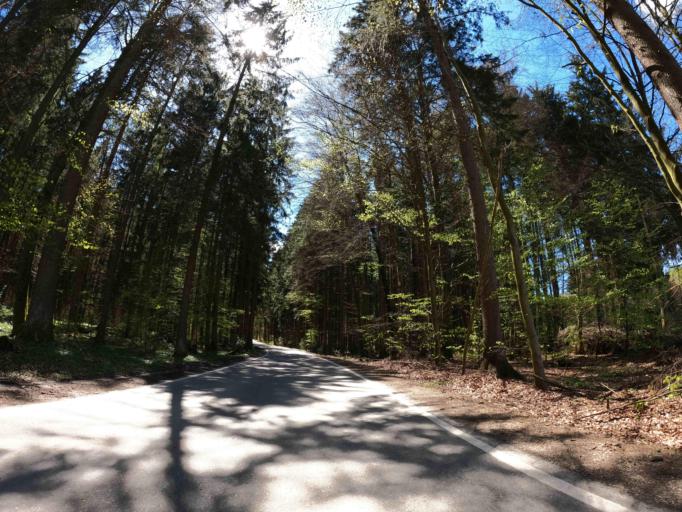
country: DE
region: Bavaria
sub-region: Upper Bavaria
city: Strasslach-Dingharting
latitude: 47.9898
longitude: 11.5460
